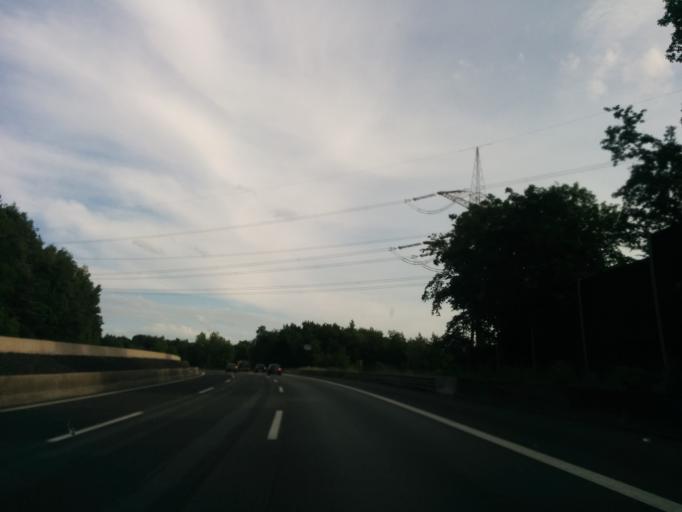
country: DE
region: Hesse
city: Schwarzenborn
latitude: 50.9664
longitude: 9.4794
